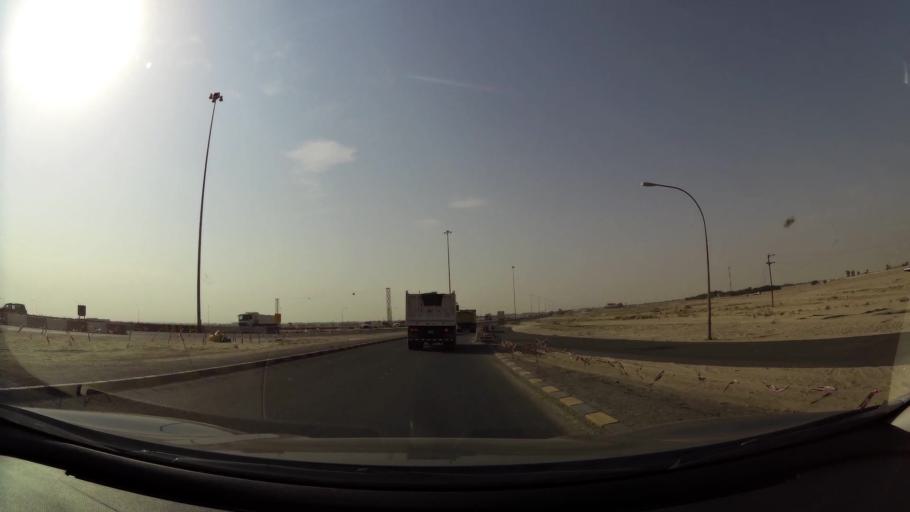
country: KW
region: Al Ahmadi
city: Al Ahmadi
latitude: 28.9572
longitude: 48.1208
